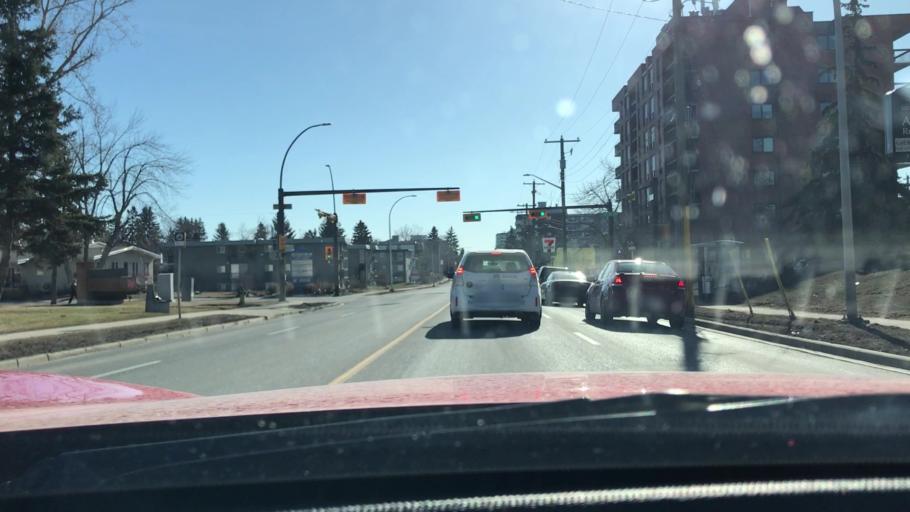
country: CA
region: Alberta
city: Calgary
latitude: 51.0378
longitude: -114.1304
